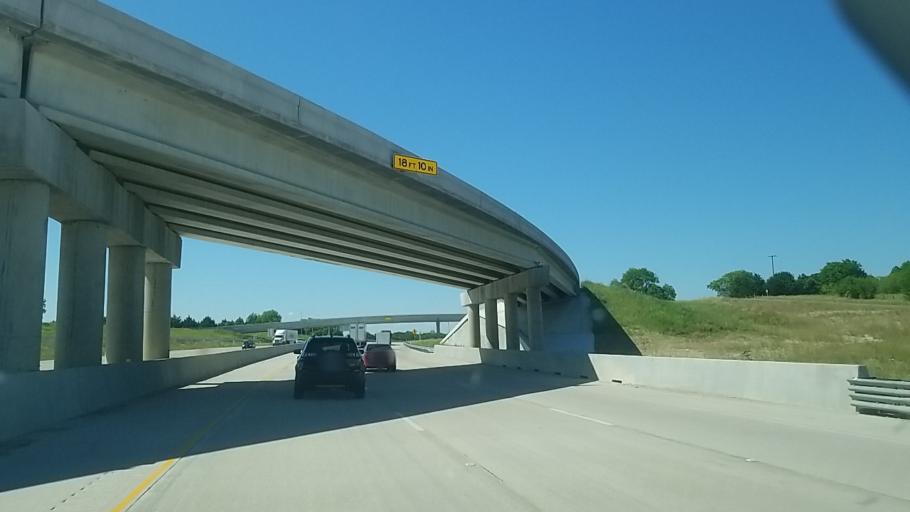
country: US
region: Texas
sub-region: Navarro County
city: Corsicana
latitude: 32.1512
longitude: -96.4670
